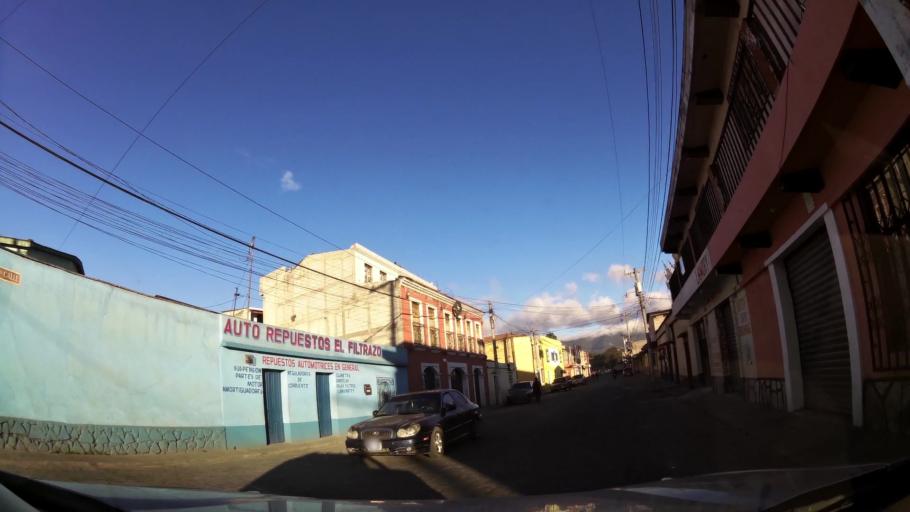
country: GT
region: Quetzaltenango
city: Quetzaltenango
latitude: 14.8349
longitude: -91.5244
